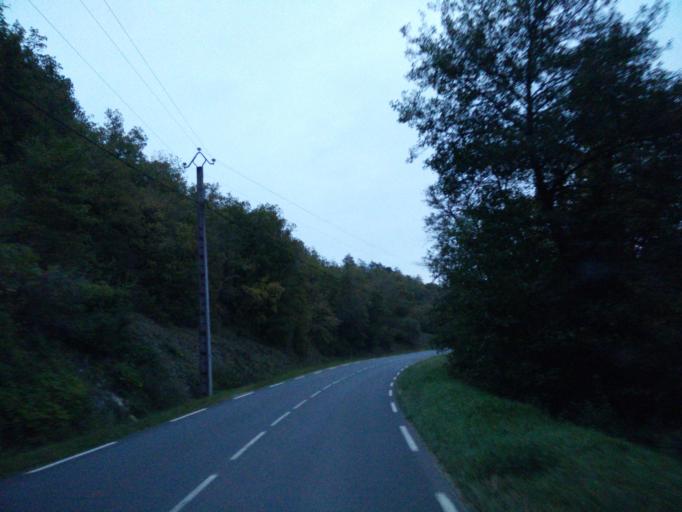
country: FR
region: Aquitaine
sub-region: Departement de la Dordogne
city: Saint-Cyprien
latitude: 44.9324
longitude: 1.0729
